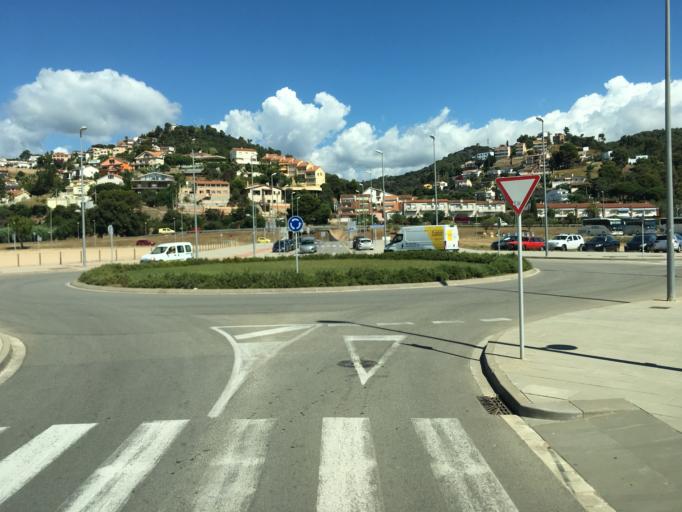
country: ES
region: Catalonia
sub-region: Provincia de Barcelona
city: Santa Susanna
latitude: 41.6381
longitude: 2.7216
